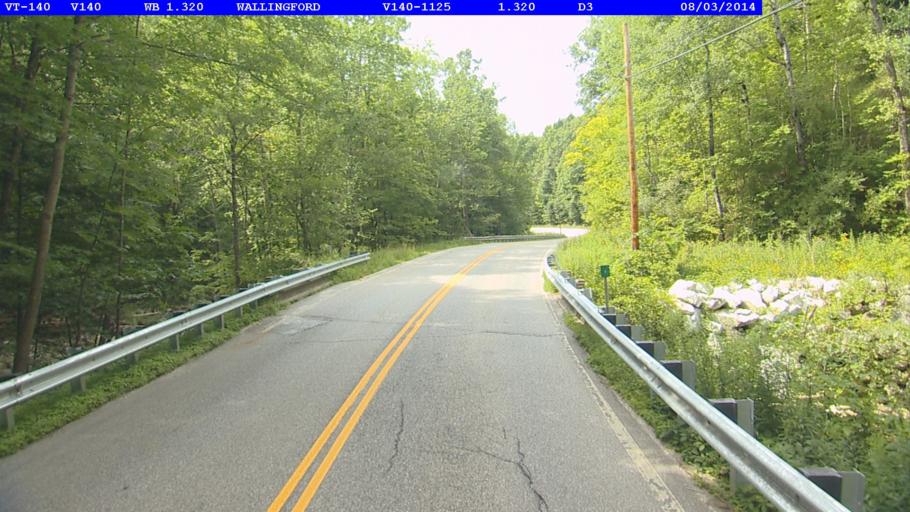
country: US
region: Vermont
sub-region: Rutland County
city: Rutland
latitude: 43.4642
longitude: -72.9545
